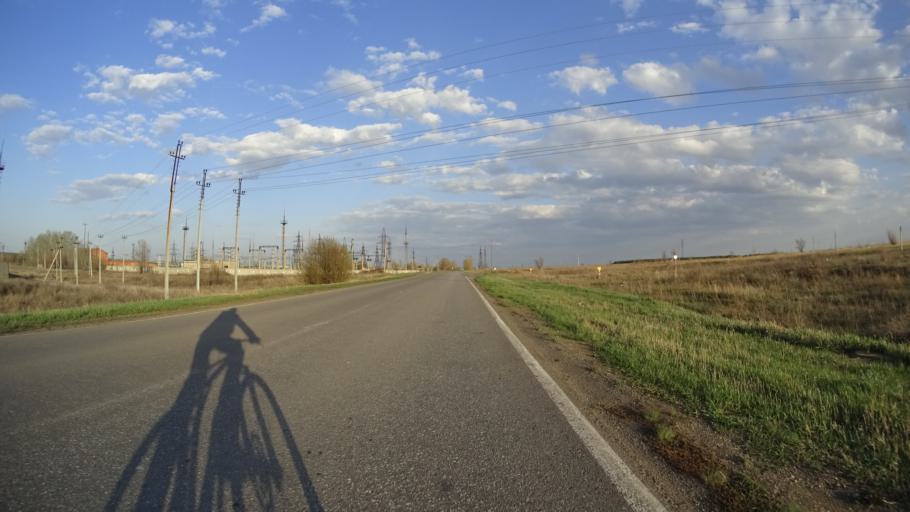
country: RU
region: Chelyabinsk
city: Troitsk
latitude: 54.0592
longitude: 61.5802
